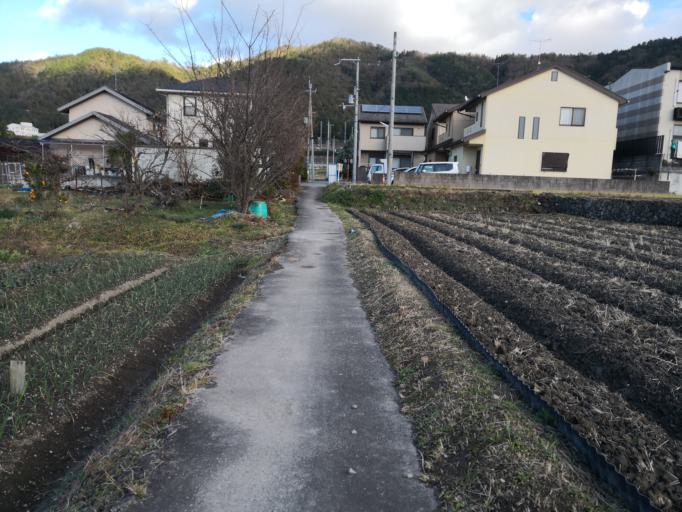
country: JP
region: Kyoto
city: Kameoka
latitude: 34.9915
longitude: 135.5486
